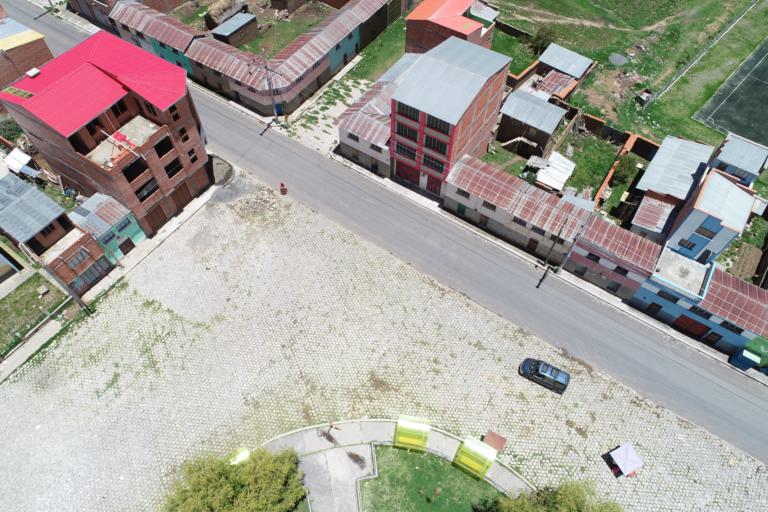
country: BO
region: La Paz
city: Achacachi
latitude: -16.0229
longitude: -68.7903
